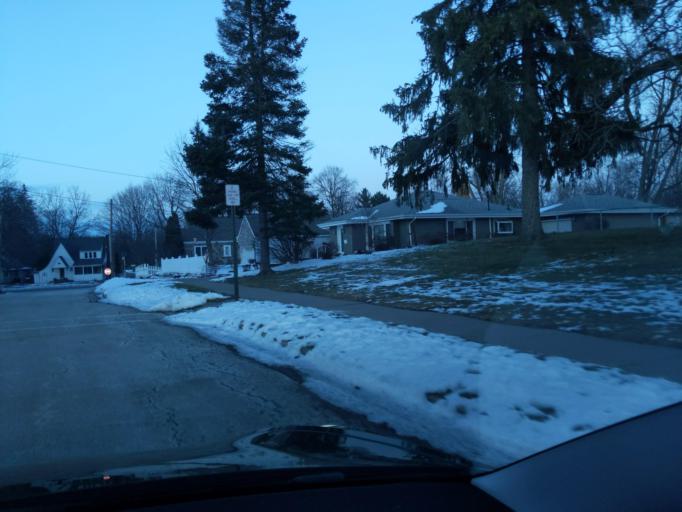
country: US
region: Michigan
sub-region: Ingham County
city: Mason
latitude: 42.5780
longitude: -84.4363
